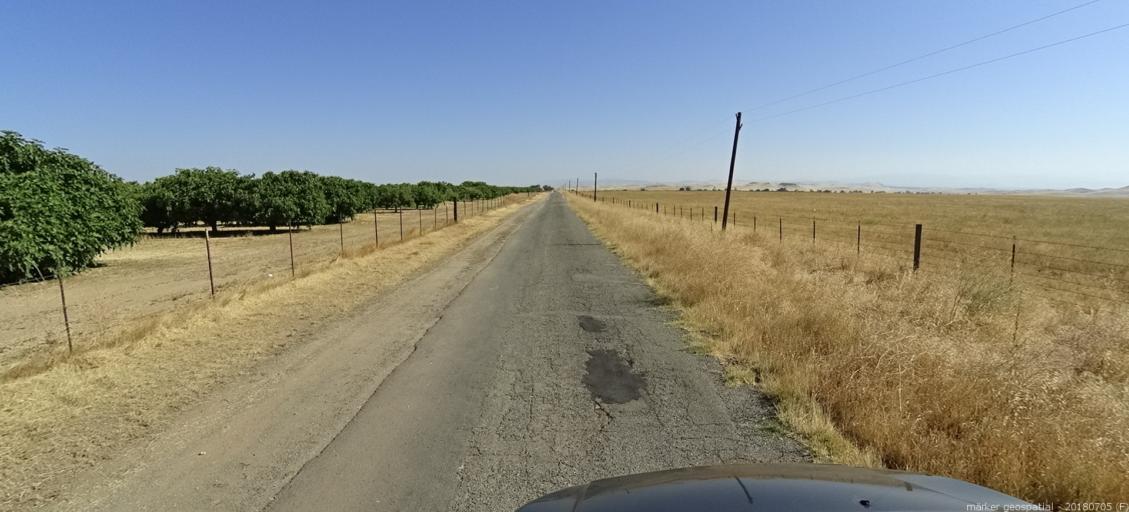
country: US
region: California
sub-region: Madera County
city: Madera Acres
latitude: 37.1525
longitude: -120.0748
